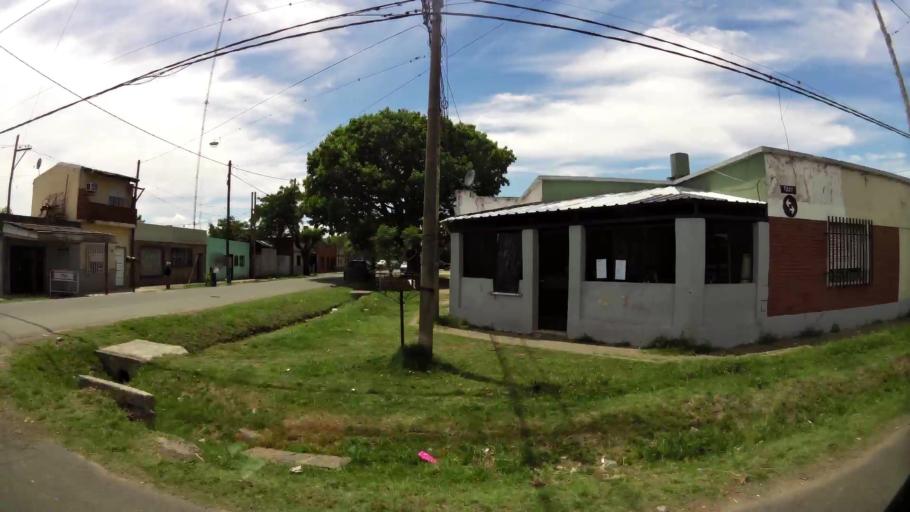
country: AR
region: Santa Fe
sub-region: Departamento de Rosario
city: Rosario
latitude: -32.9857
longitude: -60.6267
